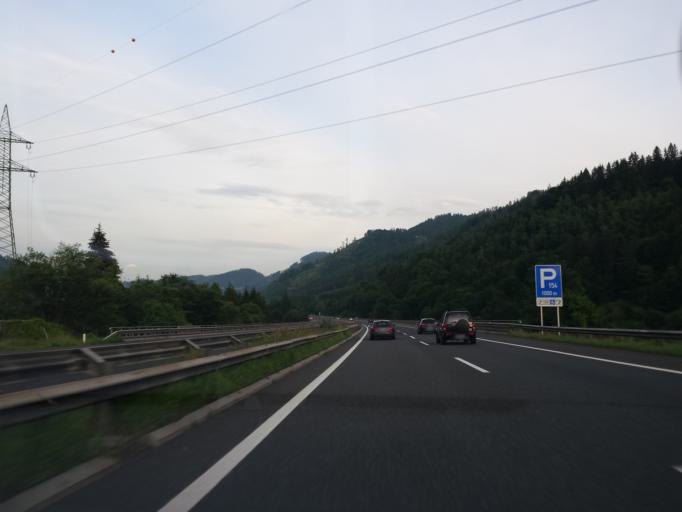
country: AT
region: Styria
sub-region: Politischer Bezirk Graz-Umgebung
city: Ubelbach
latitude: 47.2319
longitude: 15.2140
